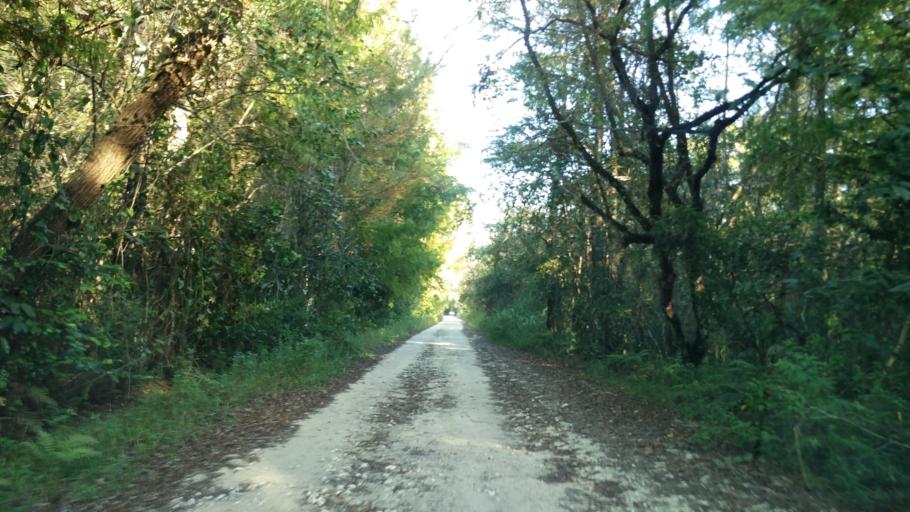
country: US
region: Florida
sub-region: Collier County
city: Lely Resort
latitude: 25.9800
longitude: -81.4032
